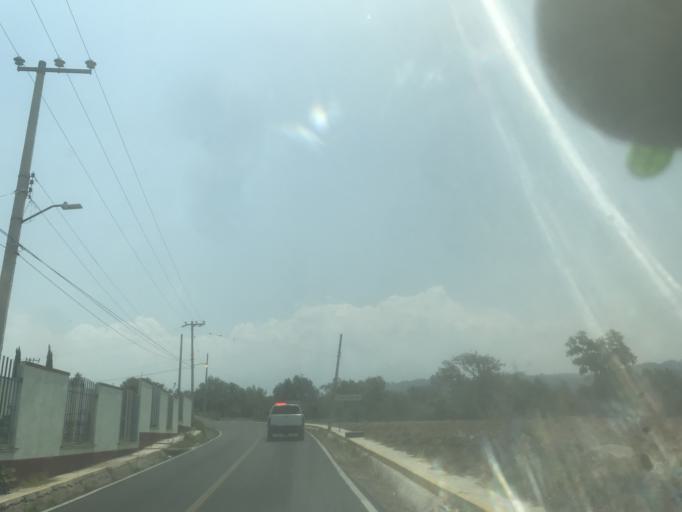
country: MX
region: Mexico
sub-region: Atlautla
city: San Andres Tlalamac
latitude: 18.9650
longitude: -98.8208
